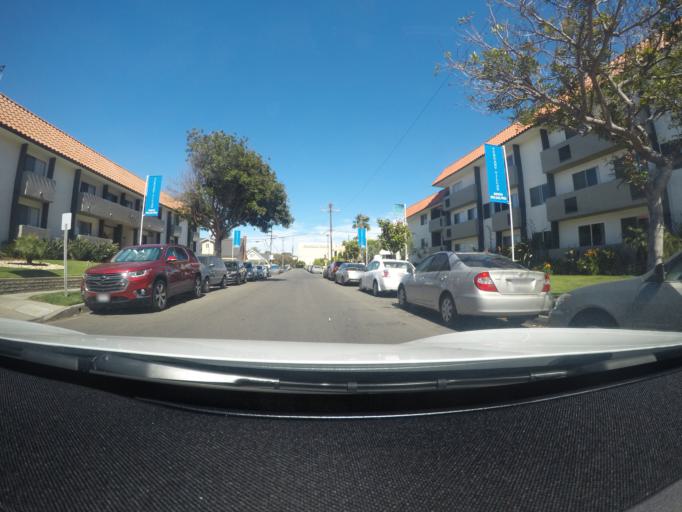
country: US
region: California
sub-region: Los Angeles County
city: Torrance
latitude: 33.8394
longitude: -118.3467
